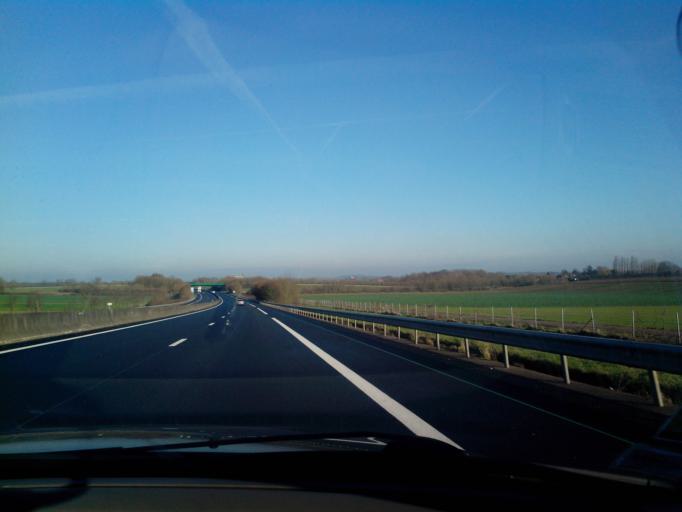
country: FR
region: Picardie
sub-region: Departement de l'Oise
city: Saint-Sulpice
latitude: 49.3336
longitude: 2.1008
